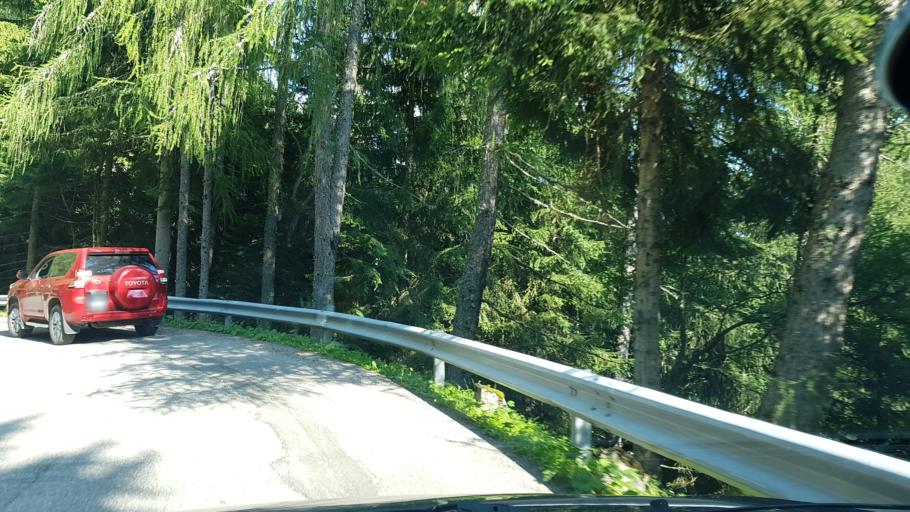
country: IT
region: Friuli Venezia Giulia
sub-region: Provincia di Udine
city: Sauris di Sotto
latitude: 46.4726
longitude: 12.6716
